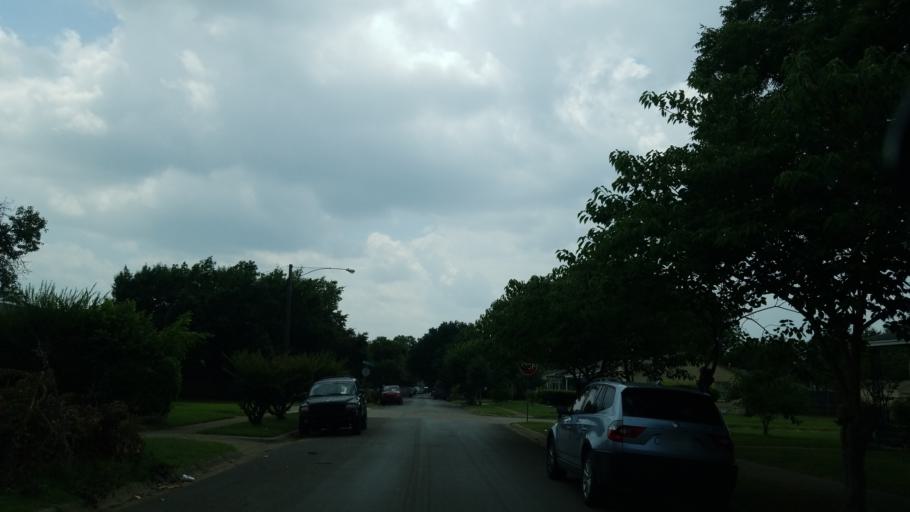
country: US
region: Texas
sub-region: Dallas County
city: University Park
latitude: 32.8494
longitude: -96.8325
